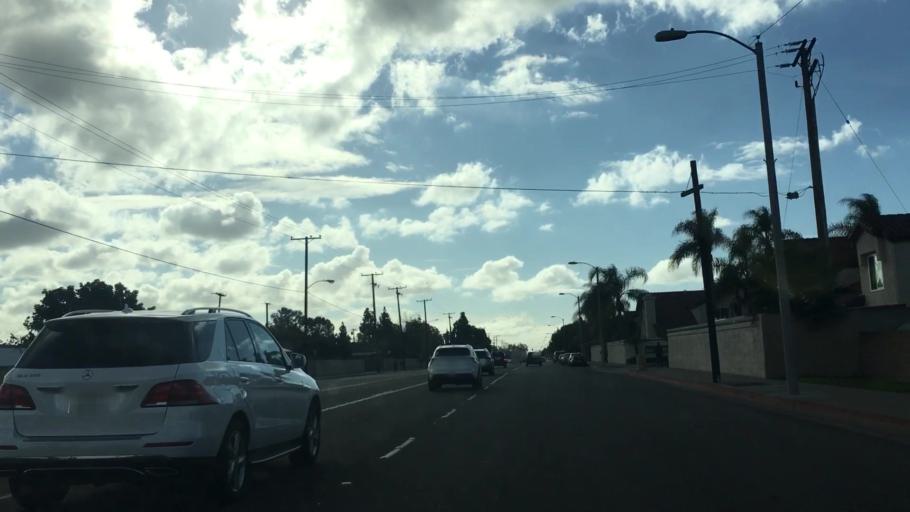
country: US
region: California
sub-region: Orange County
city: Midway City
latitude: 33.7569
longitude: -117.9725
